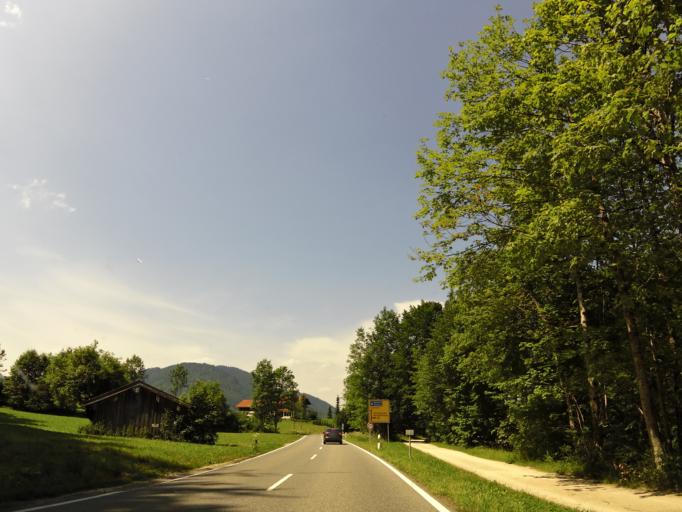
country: DE
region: Bavaria
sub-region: Upper Bavaria
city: Ruhpolding
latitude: 47.7382
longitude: 12.6594
